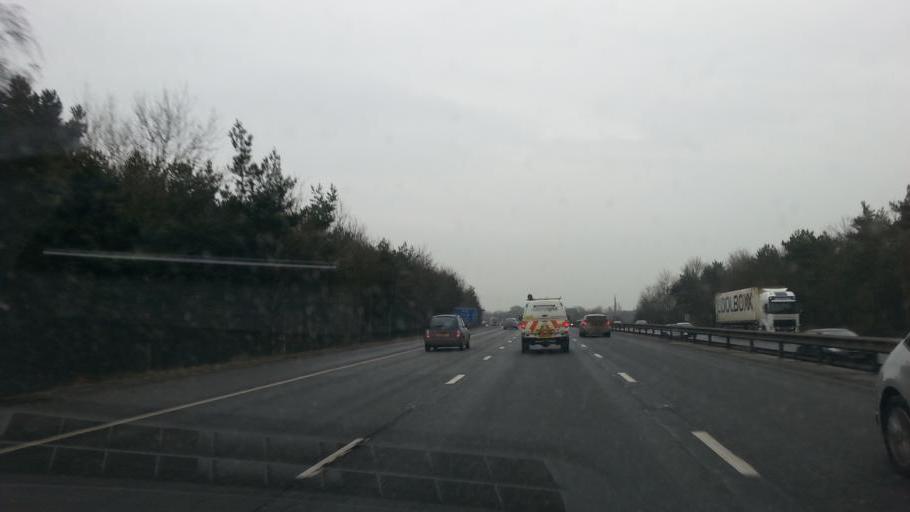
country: GB
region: England
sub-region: Essex
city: Harlow
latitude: 51.7487
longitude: 0.1424
